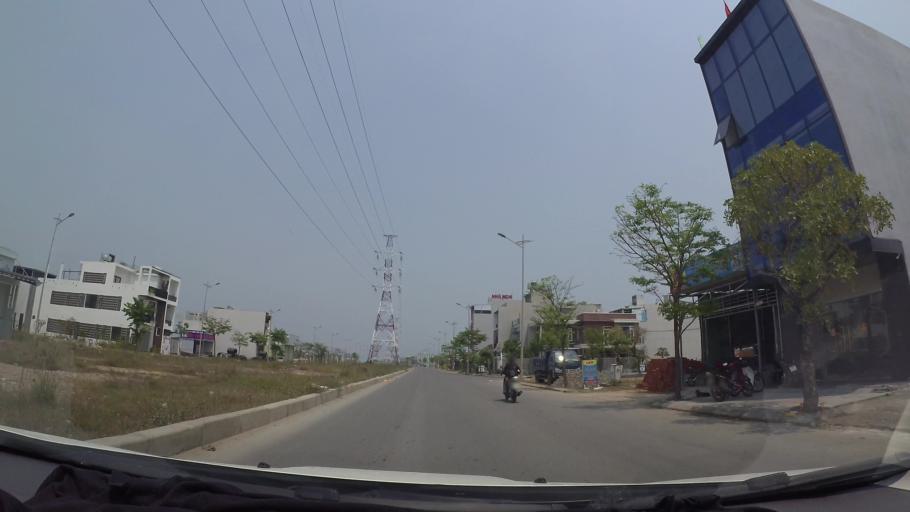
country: VN
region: Da Nang
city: Cam Le
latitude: 16.0107
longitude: 108.2233
